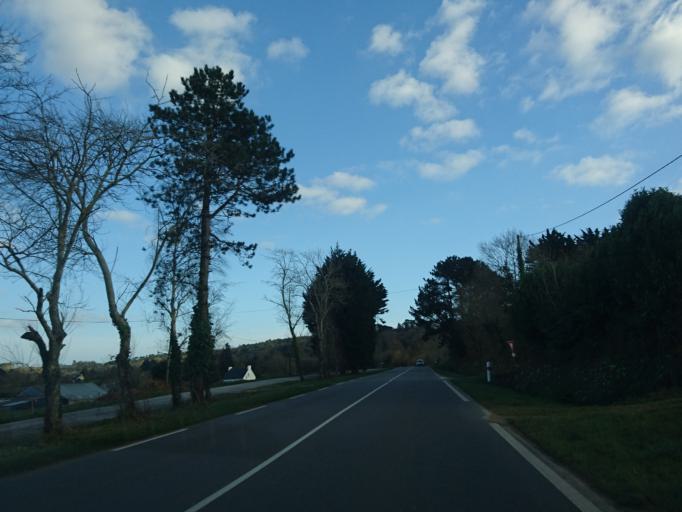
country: FR
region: Brittany
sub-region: Departement du Finistere
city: Hopital-Camfrout
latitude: 48.2818
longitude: -4.2467
